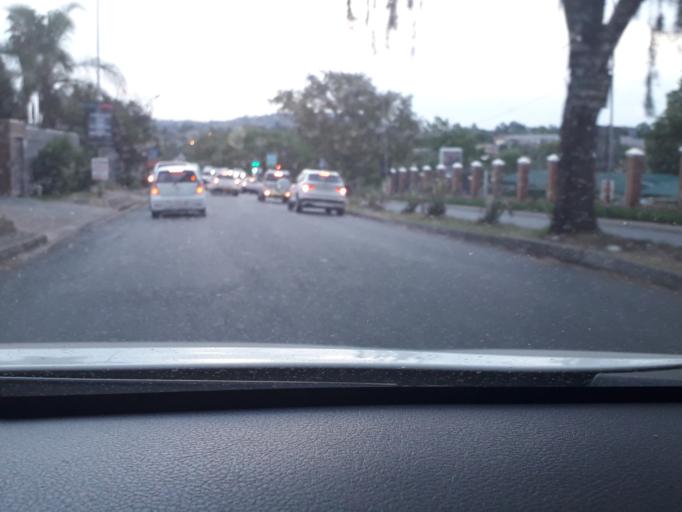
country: ZA
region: Gauteng
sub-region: City of Johannesburg Metropolitan Municipality
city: Johannesburg
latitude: -26.1430
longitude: 28.0090
